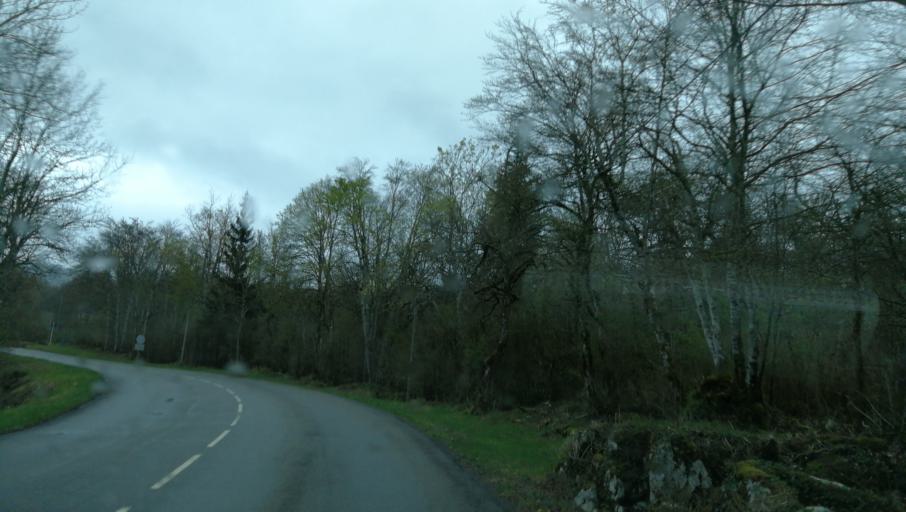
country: FR
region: Rhone-Alpes
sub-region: Departement de la Drome
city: Saint-Laurent-en-Royans
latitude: 45.0041
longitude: 5.3195
